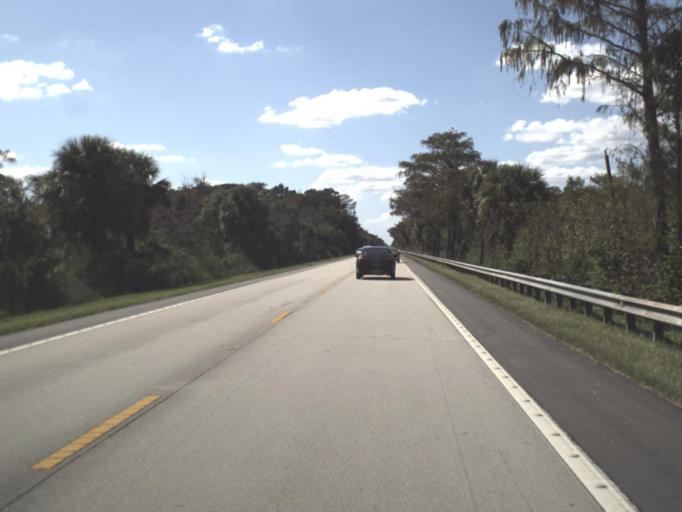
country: US
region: Florida
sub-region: Collier County
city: Marco
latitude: 25.8716
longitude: -81.1781
